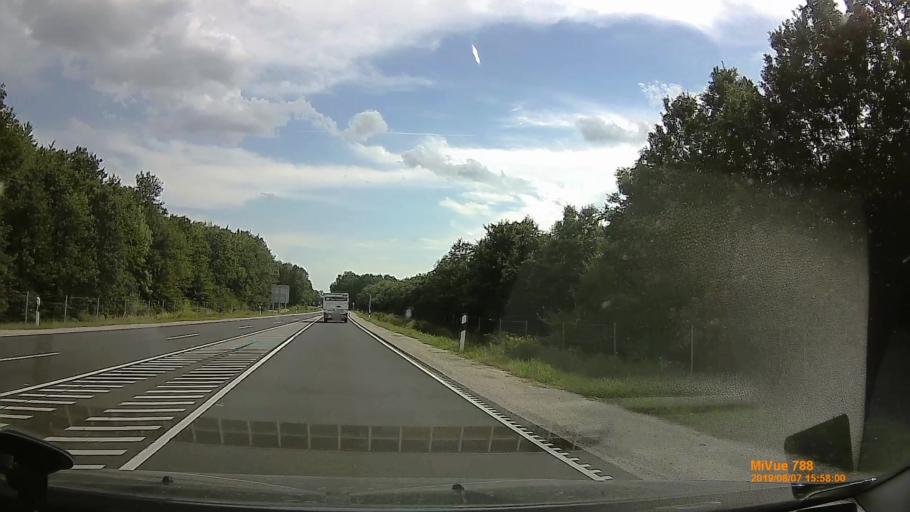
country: HU
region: Vas
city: Kormend
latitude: 47.0328
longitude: 16.6126
